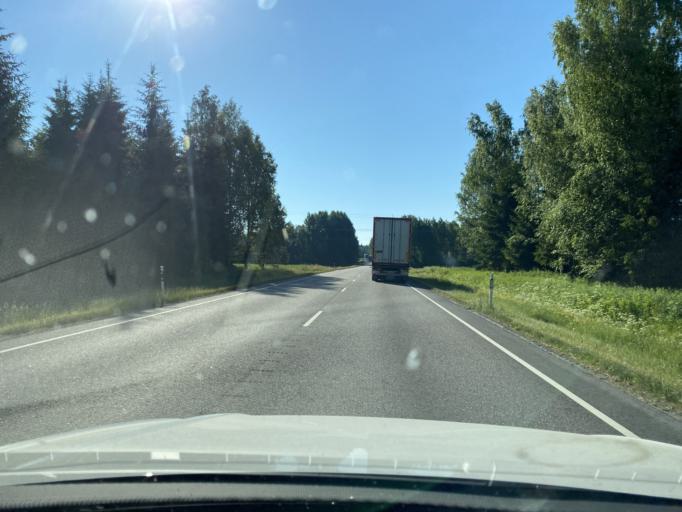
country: FI
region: Haeme
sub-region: Haemeenlinna
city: Renko
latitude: 60.7851
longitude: 24.1458
